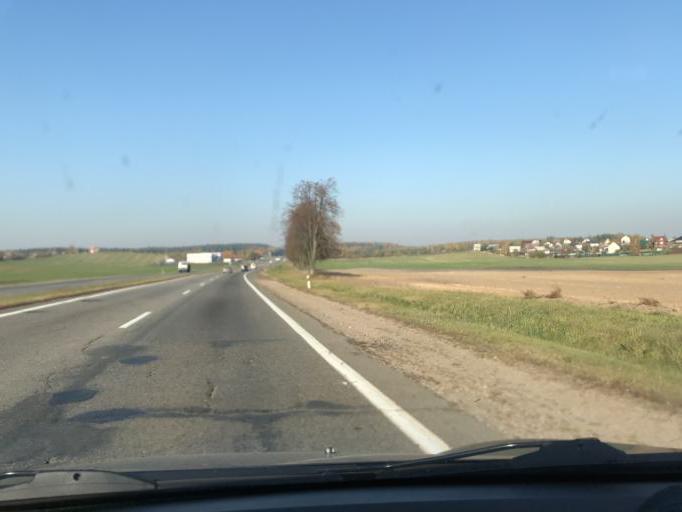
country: BY
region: Minsk
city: Luhavaya Slabada
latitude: 53.7508
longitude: 27.8332
